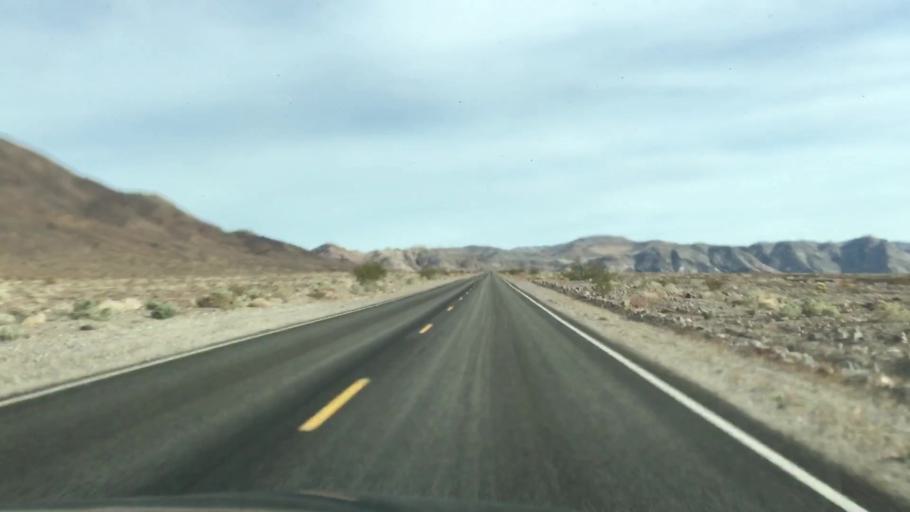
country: US
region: Nevada
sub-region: Nye County
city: Beatty
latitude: 36.7051
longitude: -116.9937
